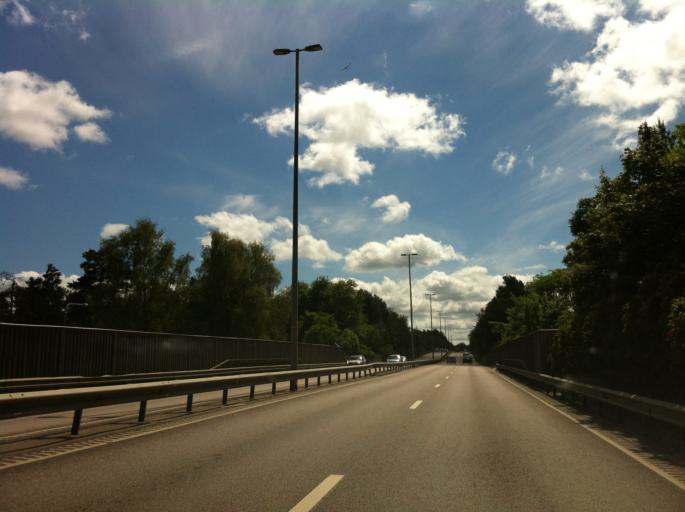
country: SE
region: Vaestra Goetaland
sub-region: Trollhattan
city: Trollhattan
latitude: 58.2947
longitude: 12.3132
